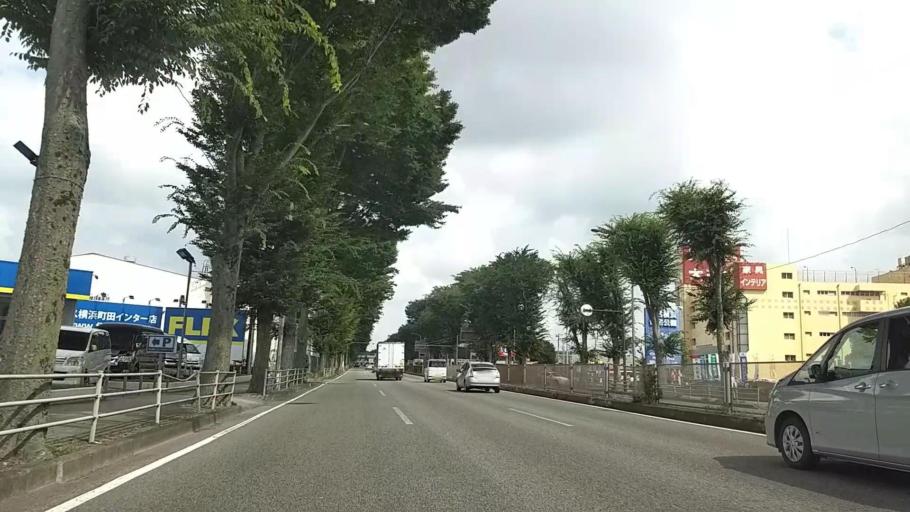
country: JP
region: Tokyo
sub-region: Machida-shi
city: Machida
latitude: 35.5190
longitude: 139.4533
